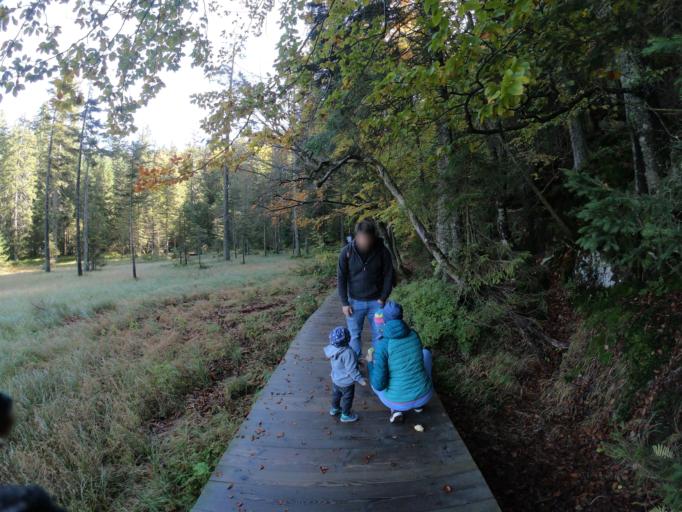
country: DE
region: Bavaria
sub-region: Lower Bavaria
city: Bayerisch Eisenstein
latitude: 49.0967
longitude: 13.1513
